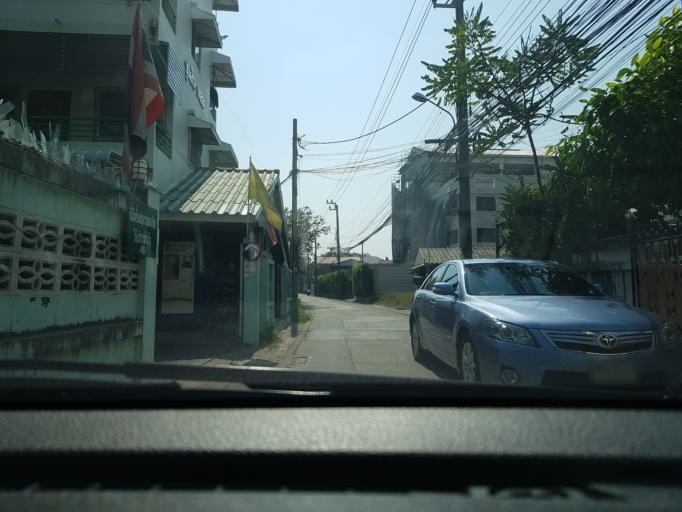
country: TH
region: Bangkok
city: Bangkok Yai
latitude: 13.7305
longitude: 100.4593
